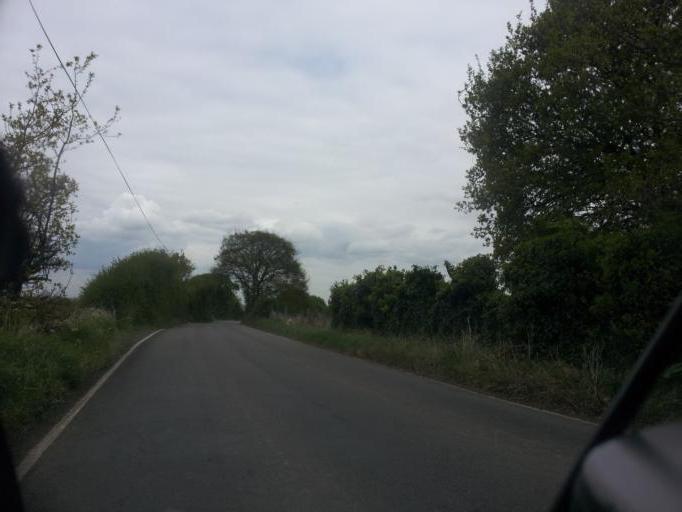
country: GB
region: England
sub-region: Kent
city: Newington
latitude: 51.3762
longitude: 0.6853
